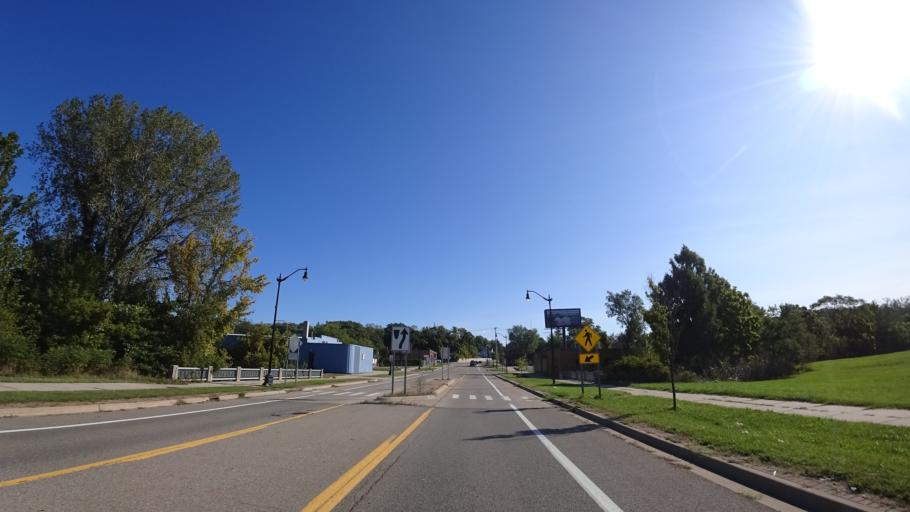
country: US
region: Michigan
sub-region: Berrien County
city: Benton Harbor
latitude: 42.1173
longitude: -86.4498
